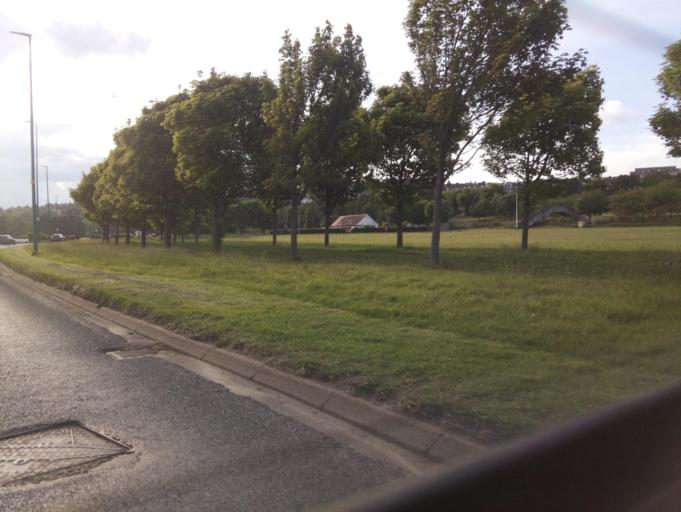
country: GB
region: Scotland
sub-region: Dundee City
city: Dundee
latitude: 56.4516
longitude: -2.9967
